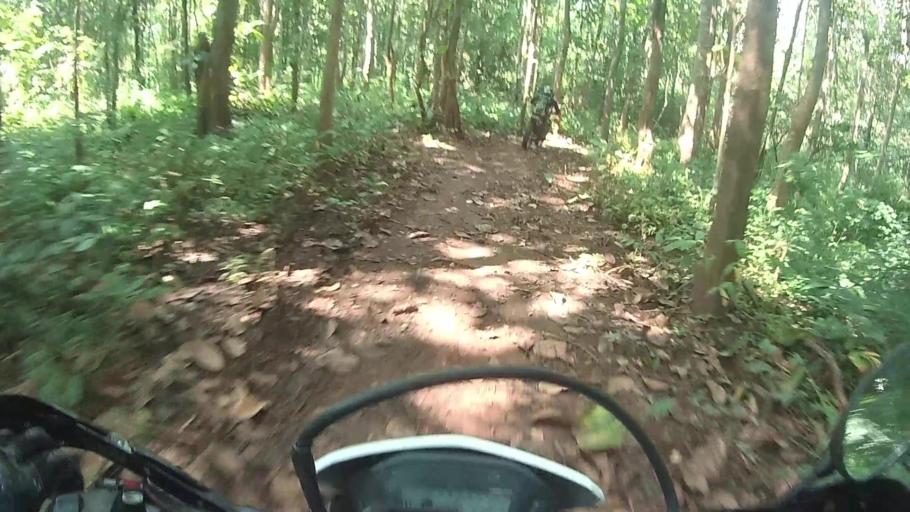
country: TH
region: Chiang Mai
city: Mae Taeng
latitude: 19.0857
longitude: 98.8330
